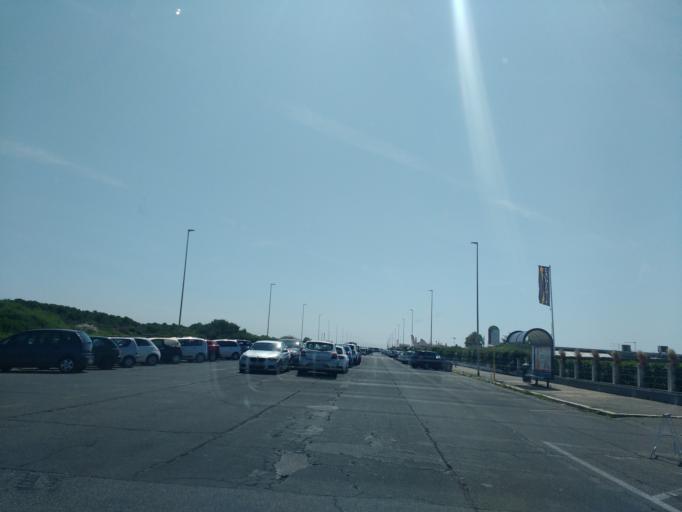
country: IT
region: Latium
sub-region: Citta metropolitana di Roma Capitale
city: Acilia-Castel Fusano-Ostia Antica
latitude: 41.7077
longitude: 12.3329
